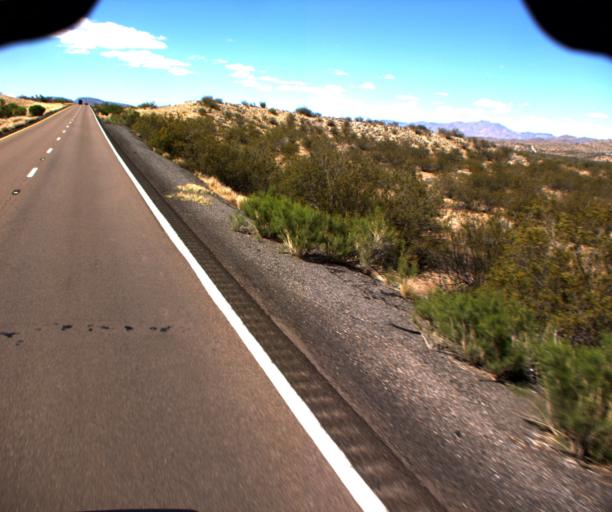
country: US
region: Arizona
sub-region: Mohave County
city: Kingman
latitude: 35.0434
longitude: -113.6646
